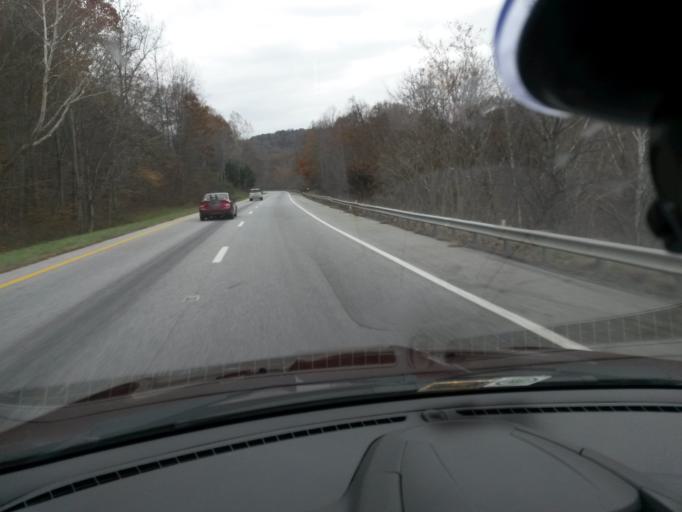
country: US
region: Virginia
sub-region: Nelson County
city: Nellysford
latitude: 37.8559
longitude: -78.7460
